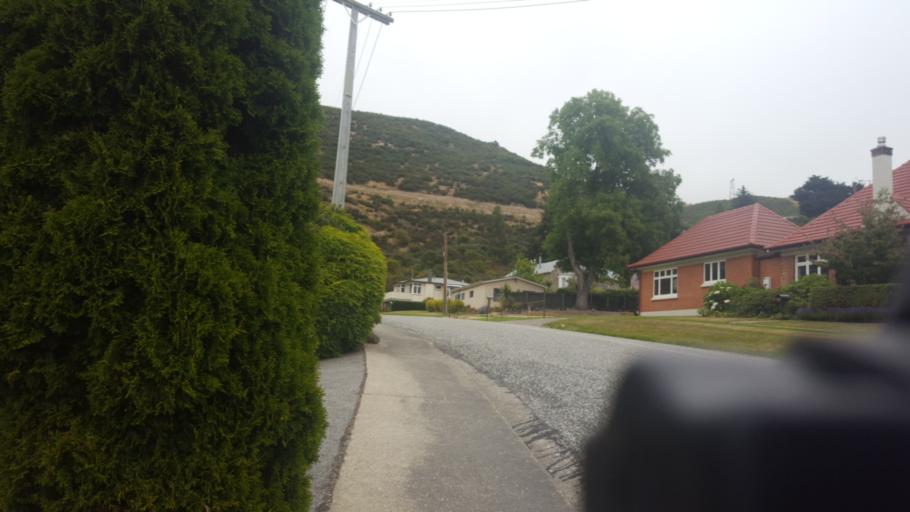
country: NZ
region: Otago
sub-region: Queenstown-Lakes District
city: Kingston
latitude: -45.5378
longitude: 169.3101
